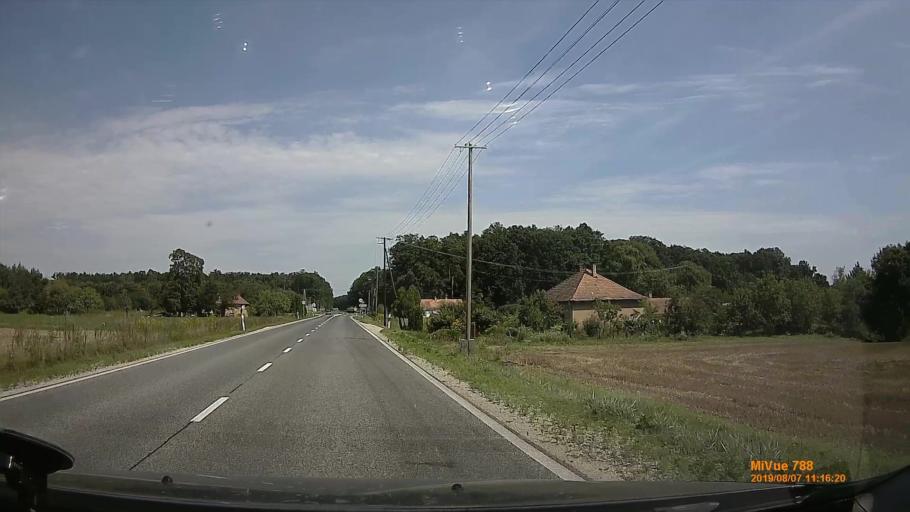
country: HU
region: Zala
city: Lenti
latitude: 46.7269
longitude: 16.5507
